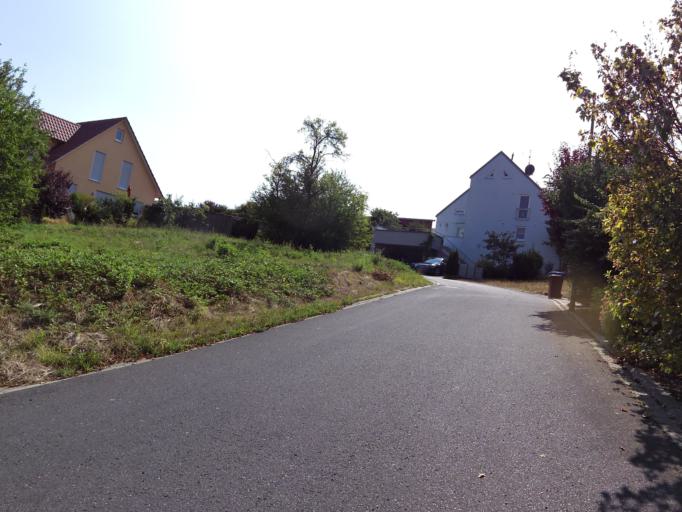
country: DE
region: Bavaria
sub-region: Regierungsbezirk Unterfranken
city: Zell am Main
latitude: 49.8128
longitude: 9.8655
